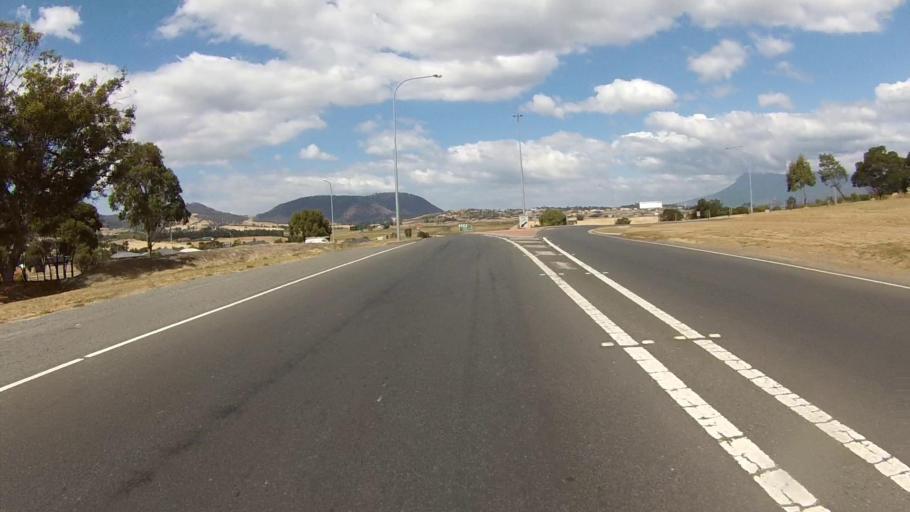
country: AU
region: Tasmania
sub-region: Glenorchy
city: Austins Ferry
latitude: -42.7502
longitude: 147.2722
